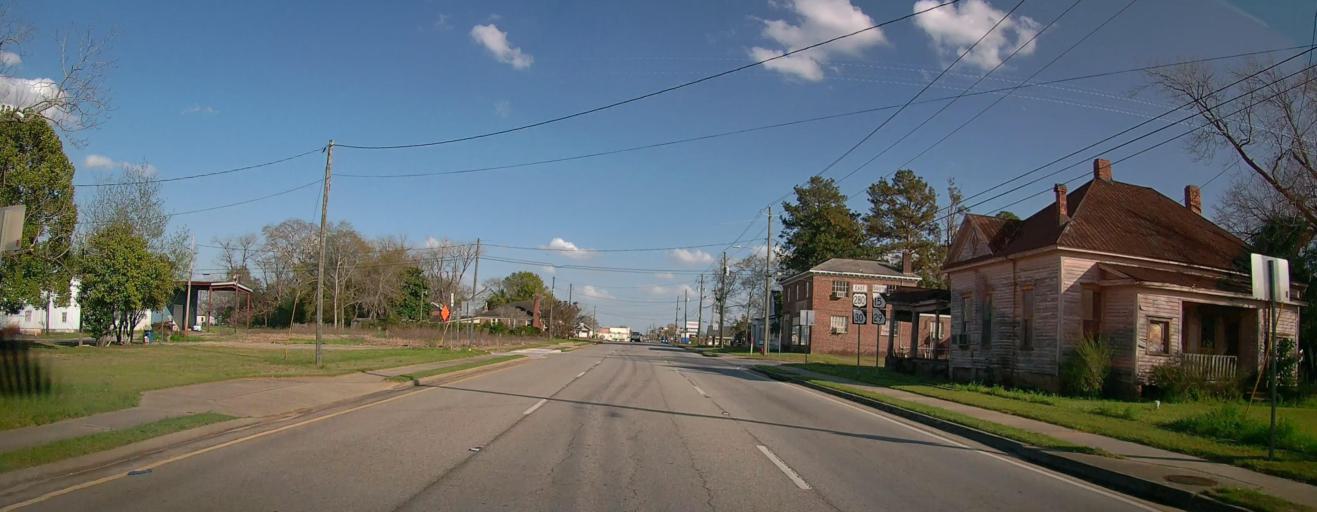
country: US
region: Georgia
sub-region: Toombs County
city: Vidalia
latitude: 32.2204
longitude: -82.4195
